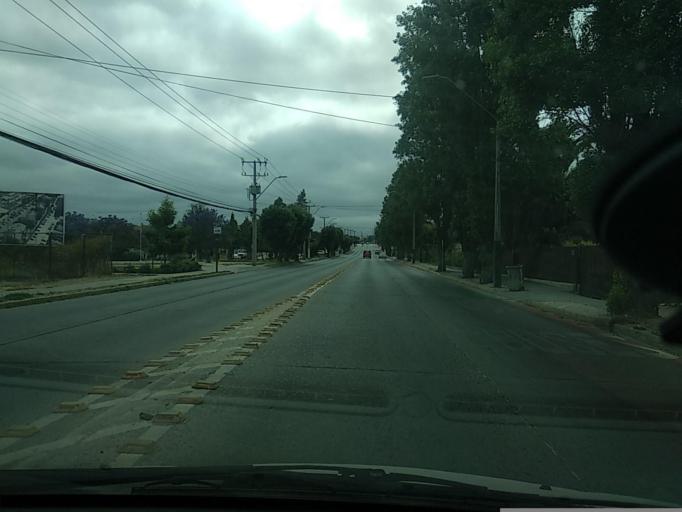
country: CL
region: Valparaiso
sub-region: Provincia de Marga Marga
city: Villa Alemana
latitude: -33.0462
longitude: -71.3960
